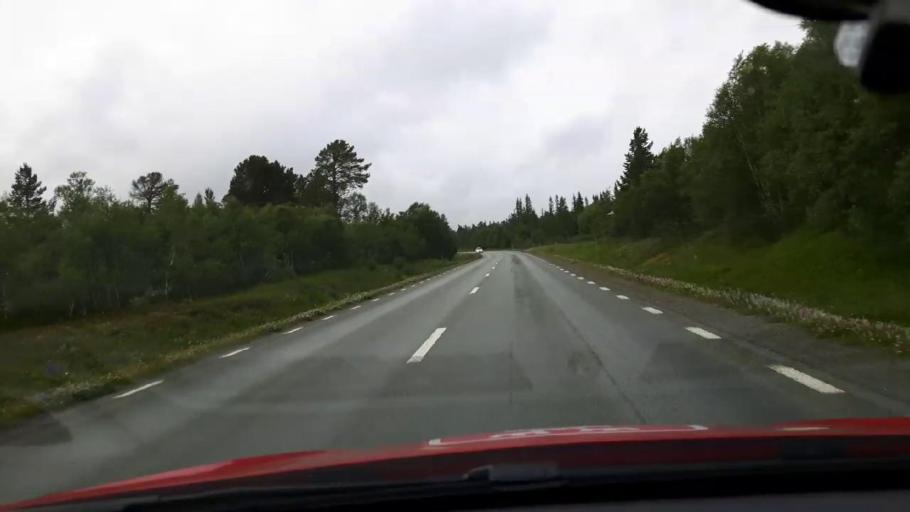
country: NO
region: Nord-Trondelag
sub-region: Meraker
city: Meraker
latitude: 63.2924
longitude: 12.1201
